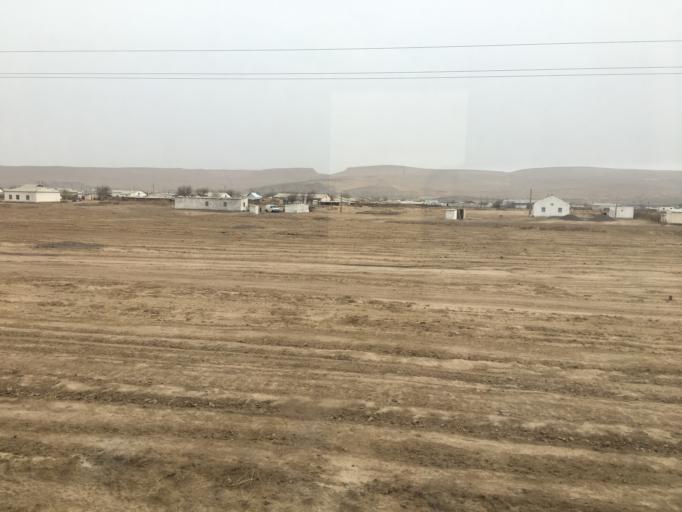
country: TM
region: Mary
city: Serhetabat
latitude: 35.5347
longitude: 62.5099
